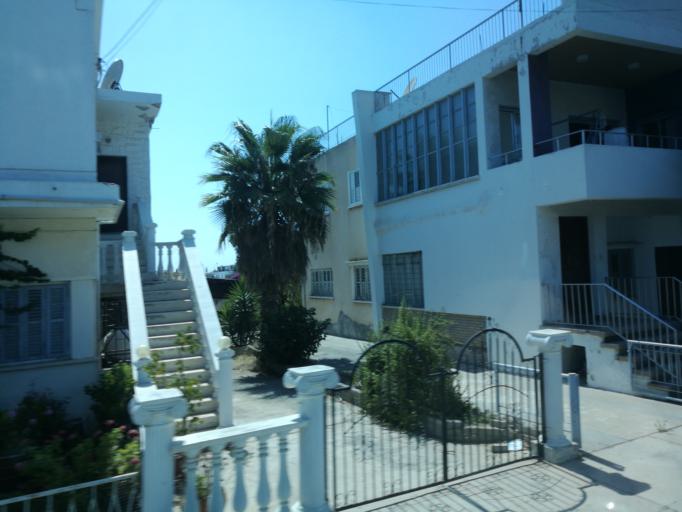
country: CY
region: Ammochostos
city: Famagusta
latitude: 35.1095
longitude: 33.9472
